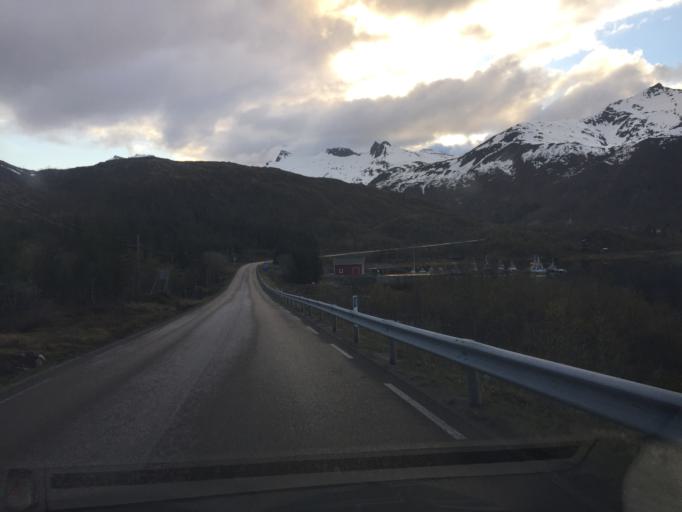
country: NO
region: Nordland
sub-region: Vagan
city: Svolvaer
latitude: 68.3182
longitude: 14.7081
